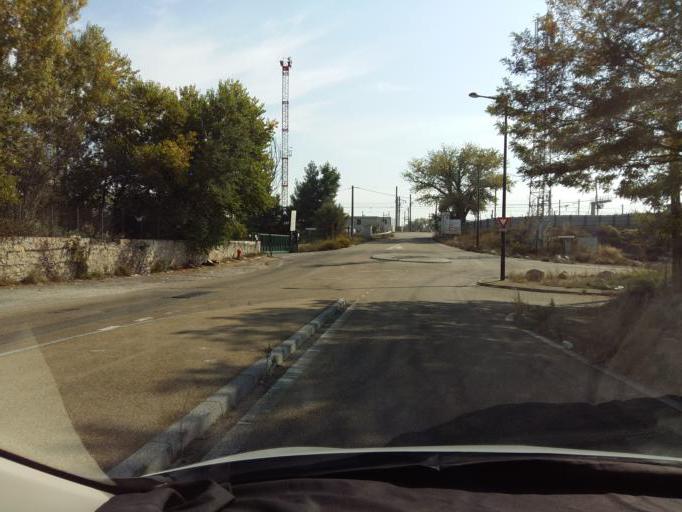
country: FR
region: Provence-Alpes-Cote d'Azur
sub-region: Departement du Vaucluse
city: Avignon
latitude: 43.9403
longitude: 4.7919
